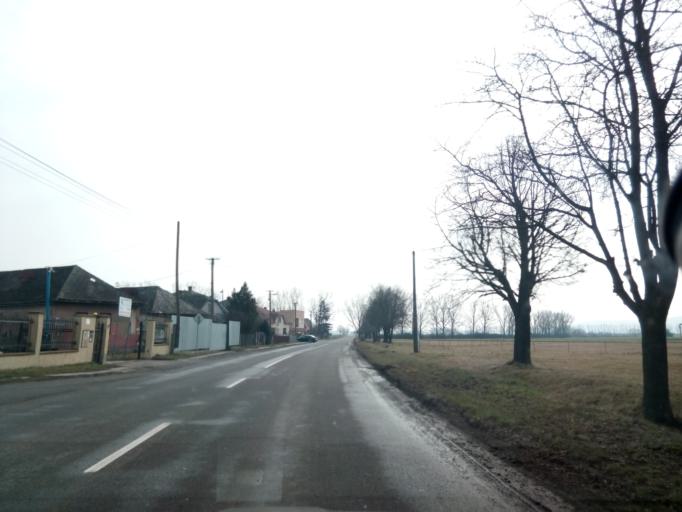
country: SK
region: Kosicky
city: Trebisov
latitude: 48.5568
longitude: 21.6740
